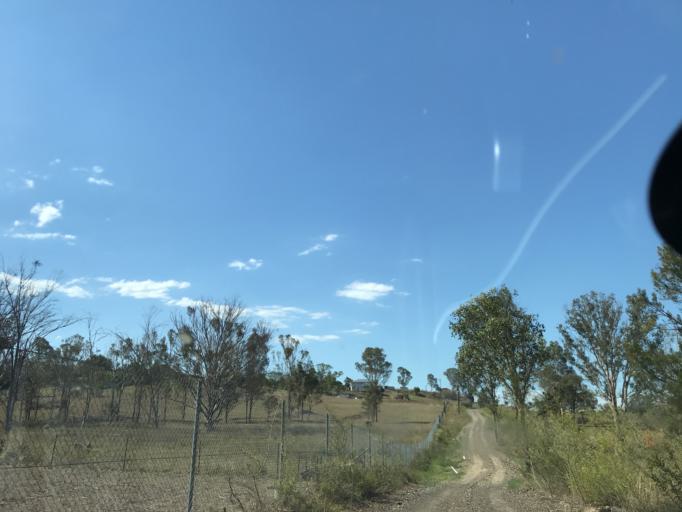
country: AU
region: New South Wales
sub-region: Penrith Municipality
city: Kingswood Park
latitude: -33.7969
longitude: 150.7367
